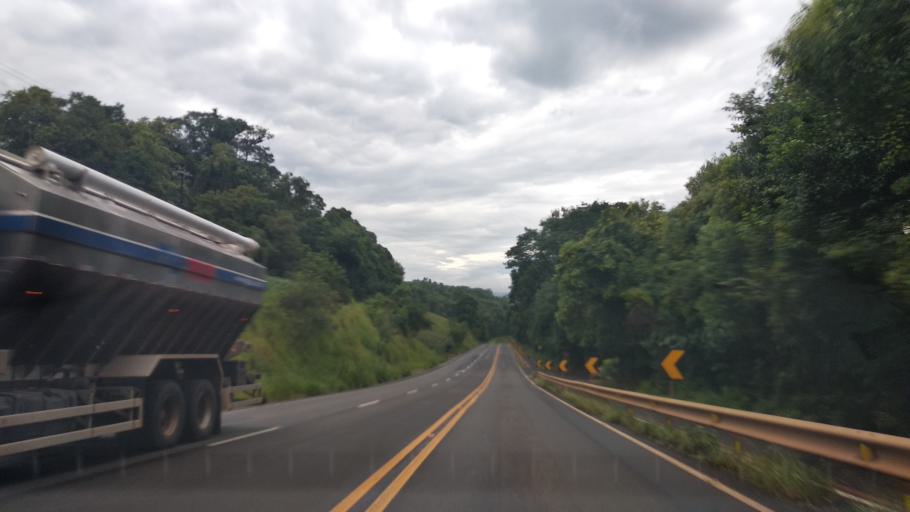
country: BR
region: Santa Catarina
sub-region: Videira
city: Videira
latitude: -27.0855
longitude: -51.2405
